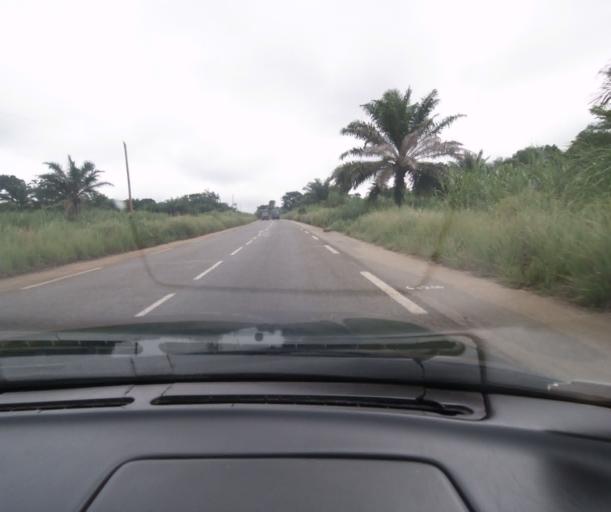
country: CM
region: Centre
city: Ombesa
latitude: 4.5697
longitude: 11.2659
